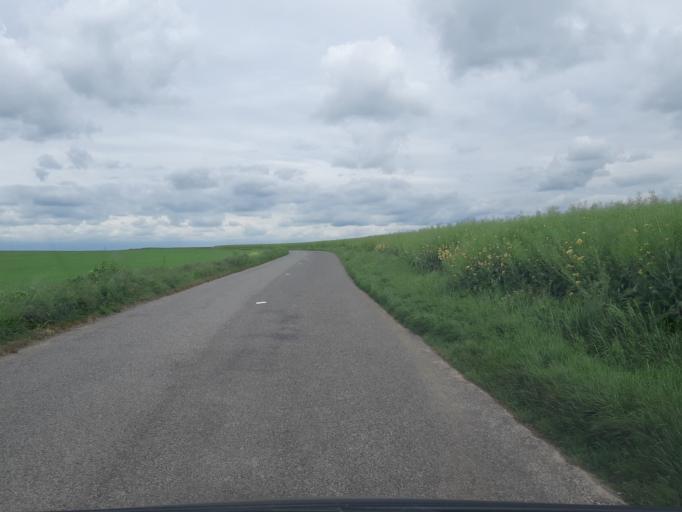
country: FR
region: Ile-de-France
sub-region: Departement de l'Essonne
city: Saclas
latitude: 48.3622
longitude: 2.1723
